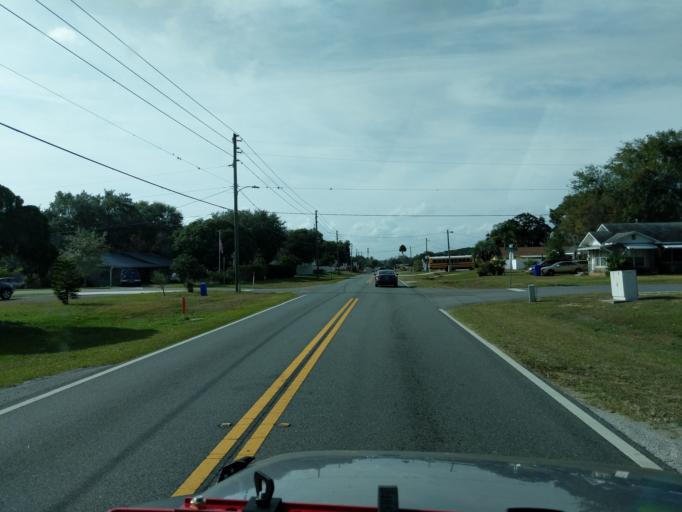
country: US
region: Florida
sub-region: Lake County
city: Tavares
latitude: 28.8040
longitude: -81.7141
